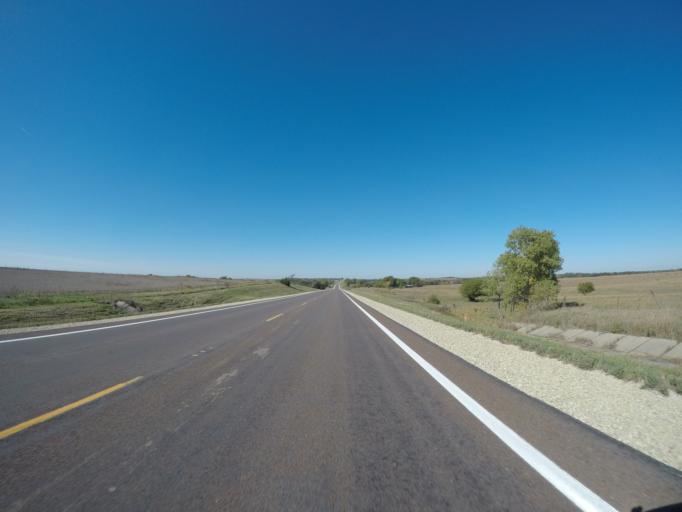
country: US
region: Kansas
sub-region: Riley County
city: Fort Riley North
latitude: 39.3065
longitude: -96.8818
